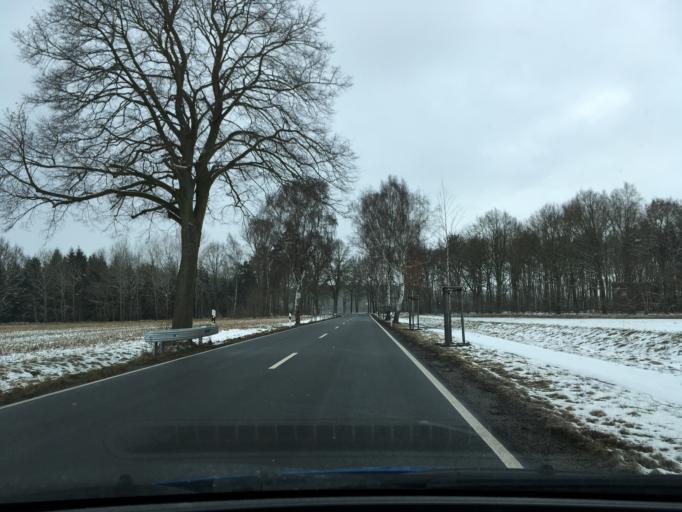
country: DE
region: Lower Saxony
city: Vierhofen
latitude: 53.2856
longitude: 10.2061
